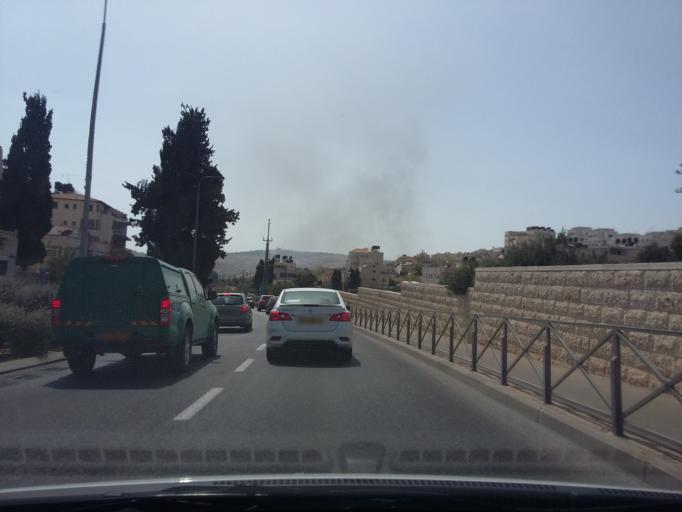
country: PS
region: West Bank
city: Ar Ram wa Dahiyat al Barid
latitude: 31.8297
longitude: 35.2251
